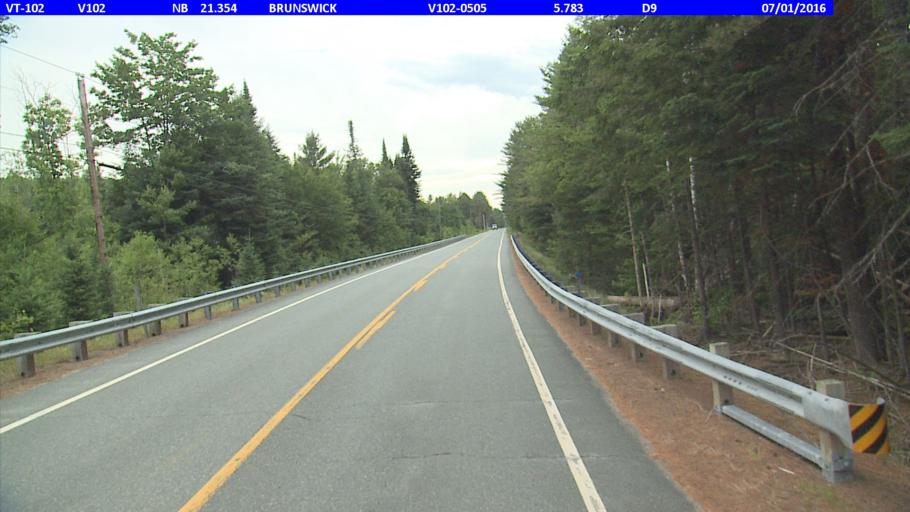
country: US
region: New Hampshire
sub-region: Coos County
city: Stratford
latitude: 44.7310
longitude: -71.6354
